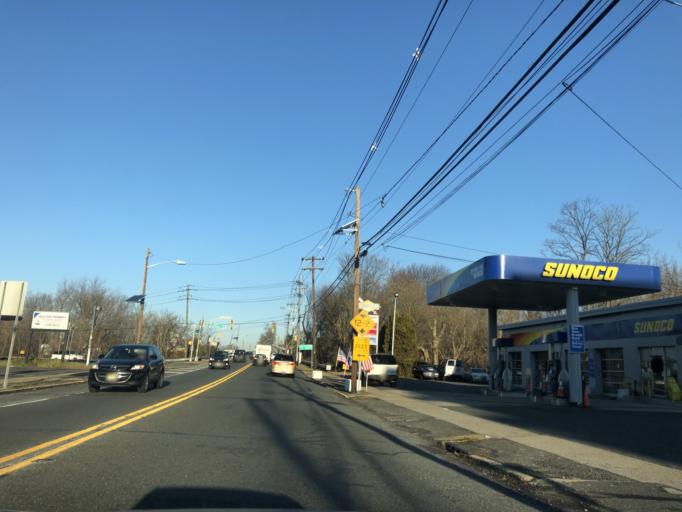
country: US
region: New Jersey
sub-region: Camden County
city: Audubon
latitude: 39.8960
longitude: -75.0707
